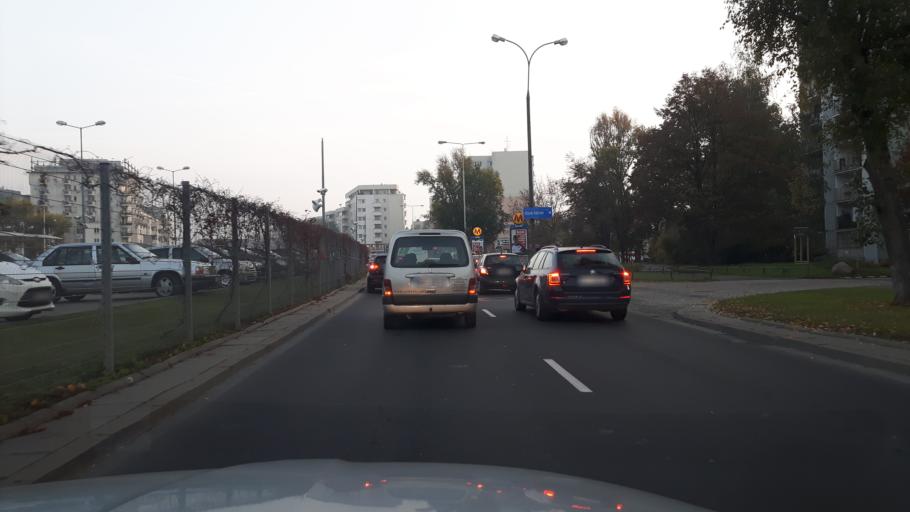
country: PL
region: Masovian Voivodeship
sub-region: Warszawa
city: Ursynow
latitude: 52.1630
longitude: 21.0270
